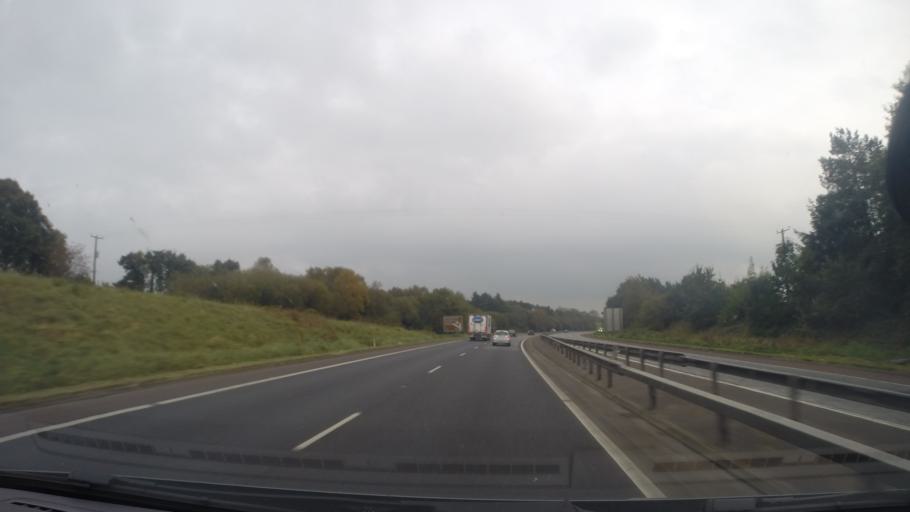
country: GB
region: Northern Ireland
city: Moy
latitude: 54.4897
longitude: -6.6338
